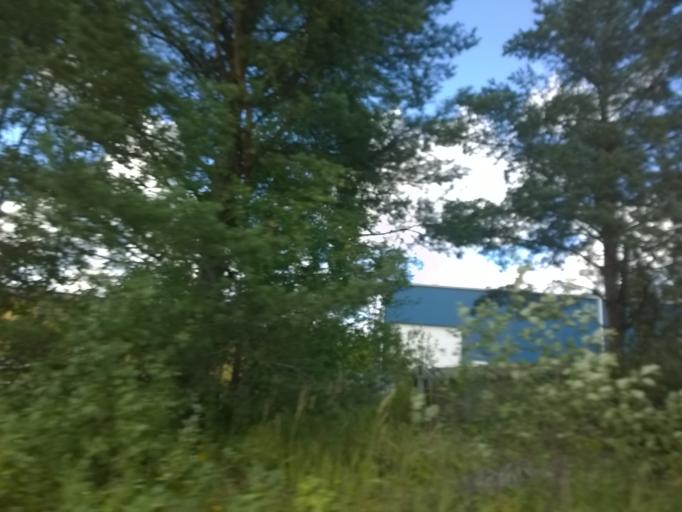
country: FI
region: Pirkanmaa
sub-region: Tampere
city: Tampere
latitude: 61.4533
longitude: 23.8953
